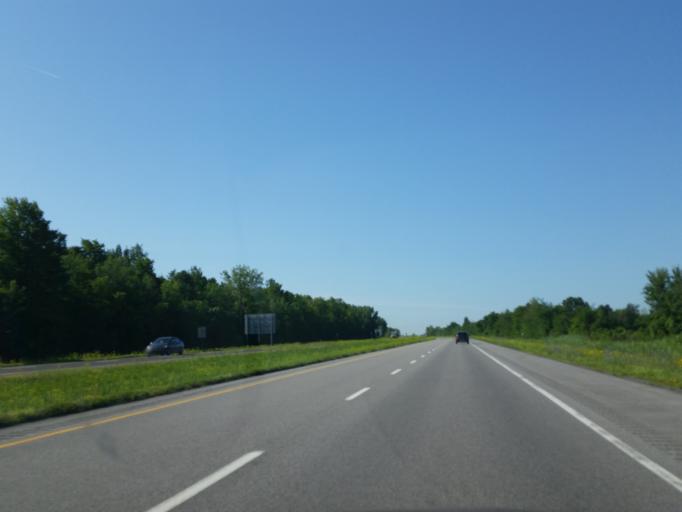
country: CA
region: Quebec
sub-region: Monteregie
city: Napierville
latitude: 45.2499
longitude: -73.4719
